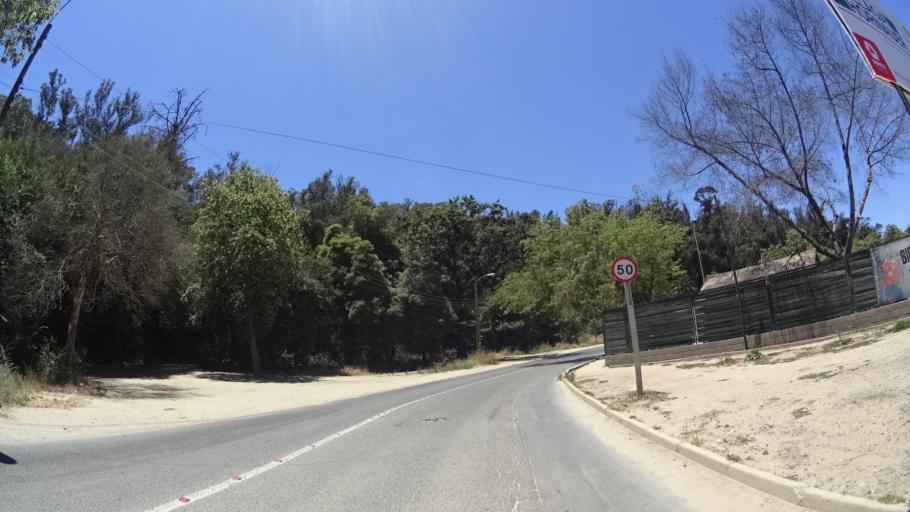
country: CL
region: Valparaiso
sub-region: Provincia de Valparaiso
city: Vina del Mar
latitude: -33.0209
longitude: -71.5363
